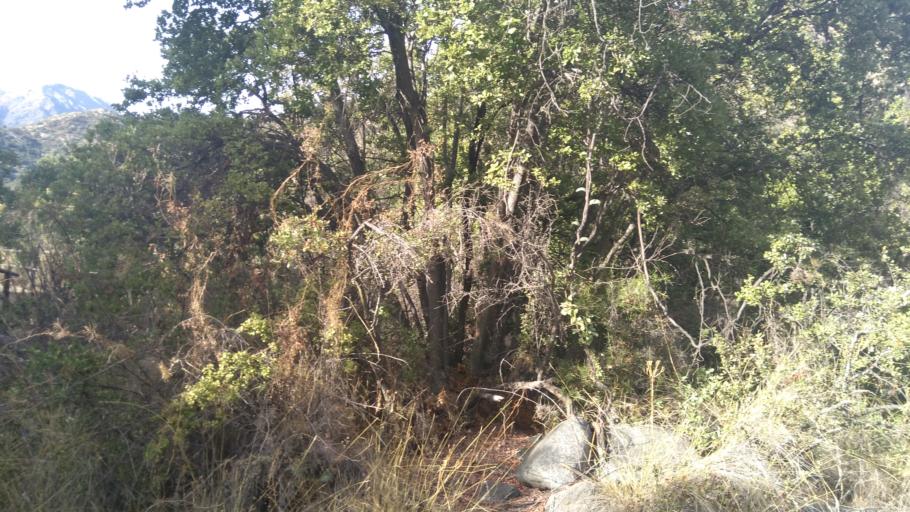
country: CL
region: Santiago Metropolitan
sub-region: Provincia de Cordillera
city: Puente Alto
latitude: -33.7242
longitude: -70.4810
